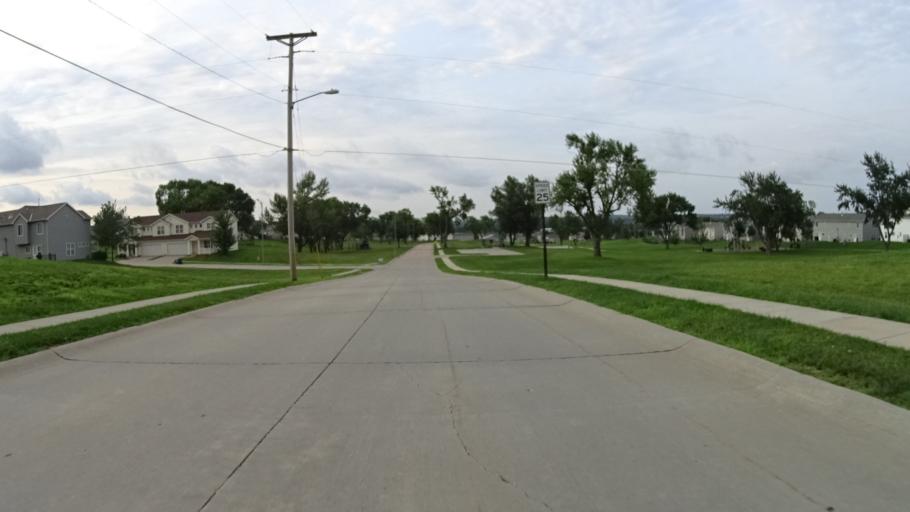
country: US
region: Nebraska
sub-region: Sarpy County
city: Offutt Air Force Base
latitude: 41.1213
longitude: -95.9538
